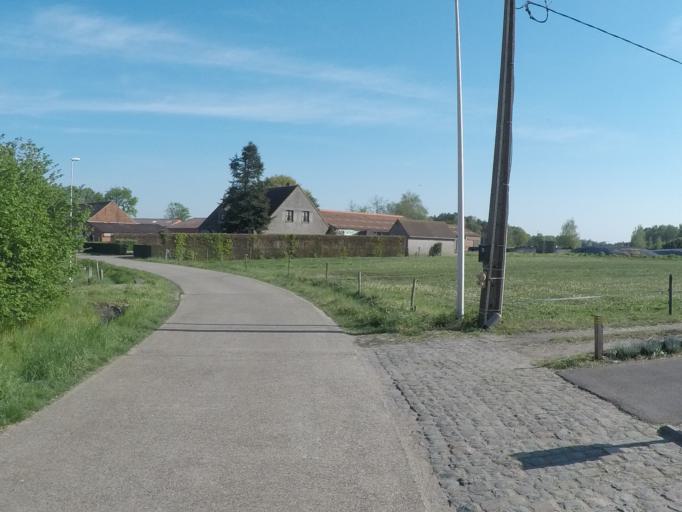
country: BE
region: Flanders
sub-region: Provincie Antwerpen
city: Nijlen
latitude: 51.1600
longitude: 4.6935
